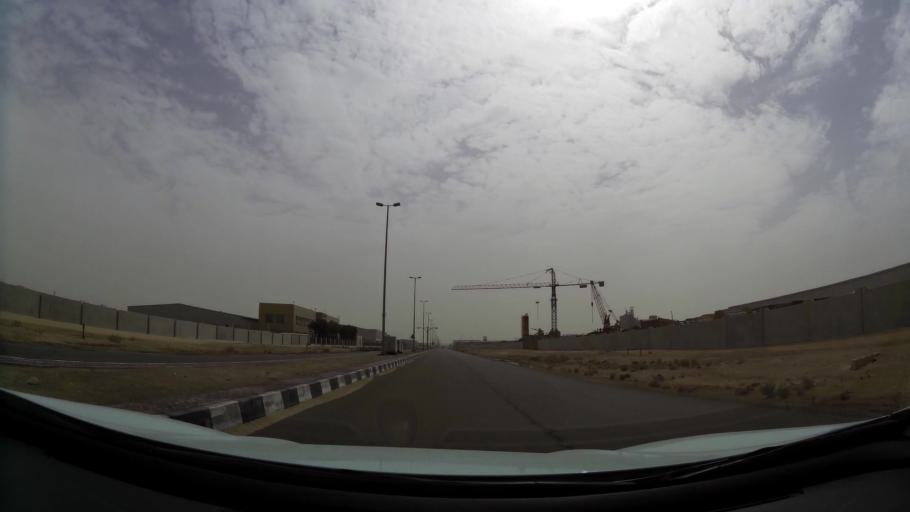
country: AE
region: Abu Dhabi
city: Abu Dhabi
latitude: 24.3337
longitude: 54.5036
